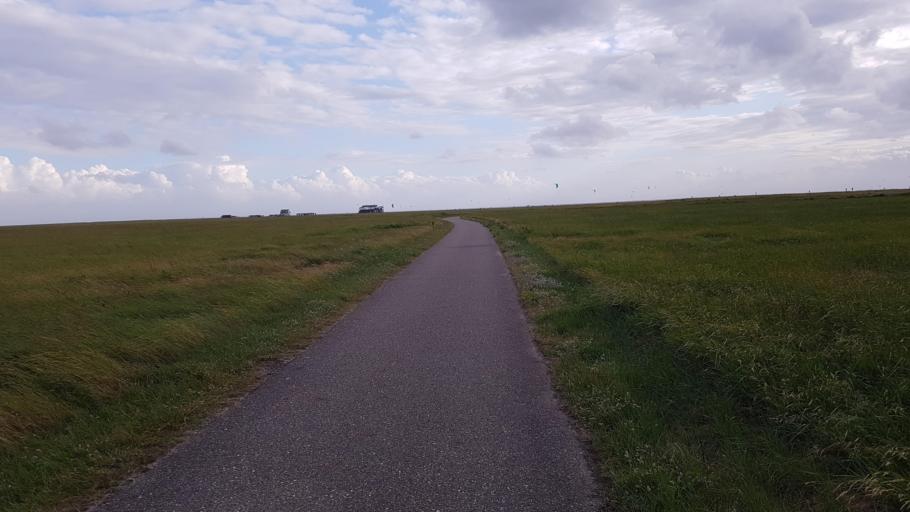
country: DE
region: Schleswig-Holstein
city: Sankt Peter-Ording
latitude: 54.2805
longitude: 8.6607
